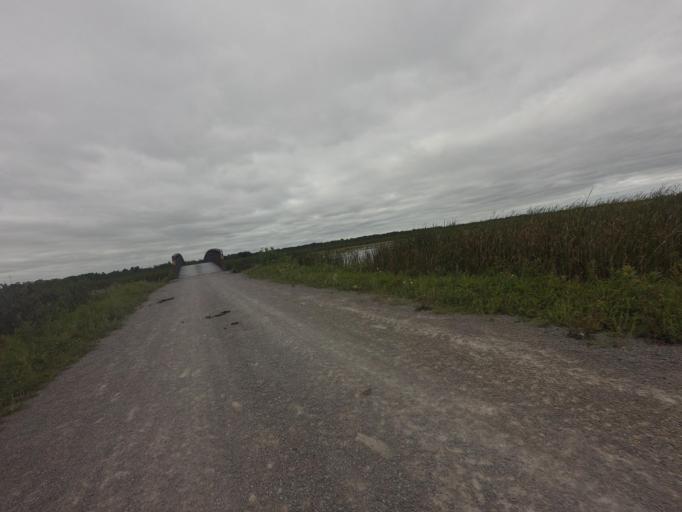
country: CA
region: Ontario
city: Omemee
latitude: 44.4113
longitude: -78.7719
